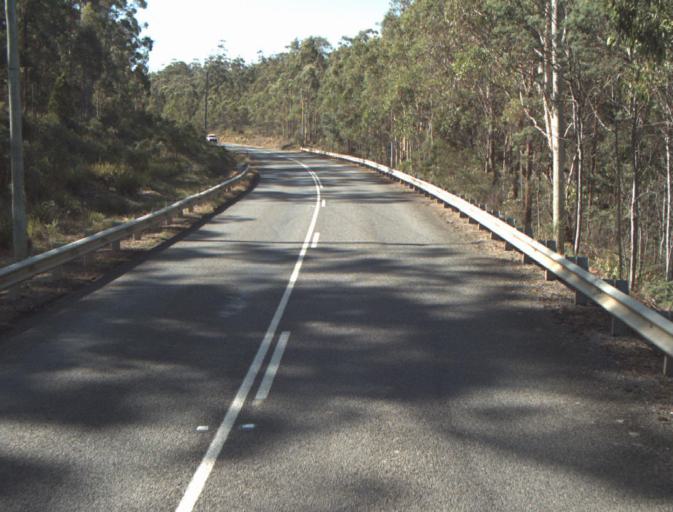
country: AU
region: Tasmania
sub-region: Launceston
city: Mayfield
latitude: -41.3252
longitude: 147.1860
